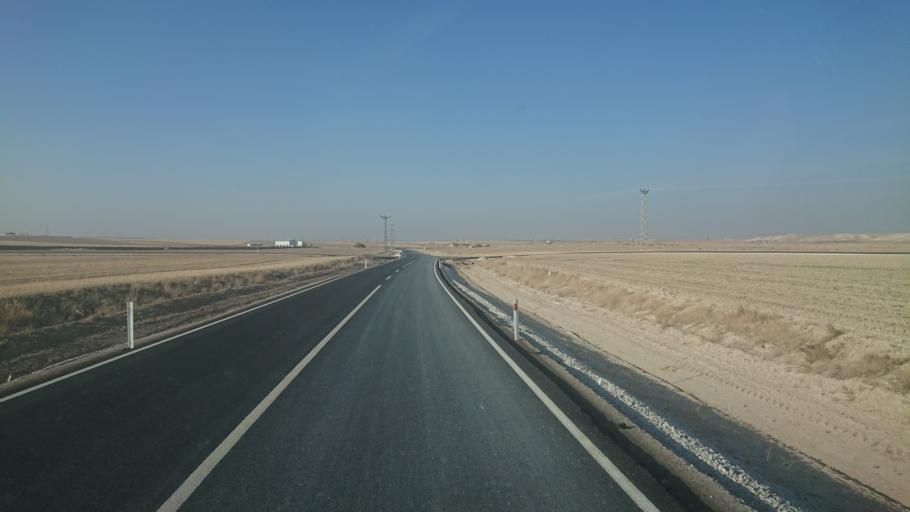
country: TR
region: Aksaray
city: Sultanhani
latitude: 38.0887
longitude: 33.6122
